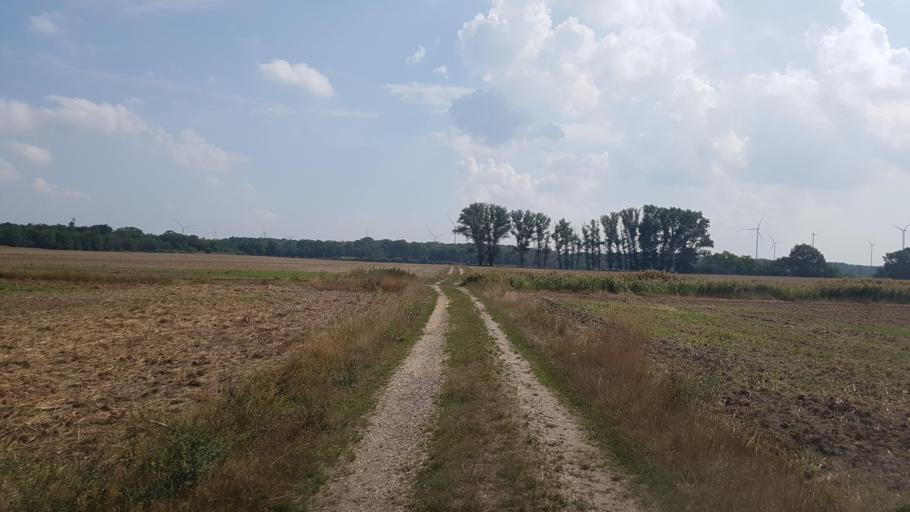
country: DE
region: Brandenburg
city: Bronkow
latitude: 51.6275
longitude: 13.9328
